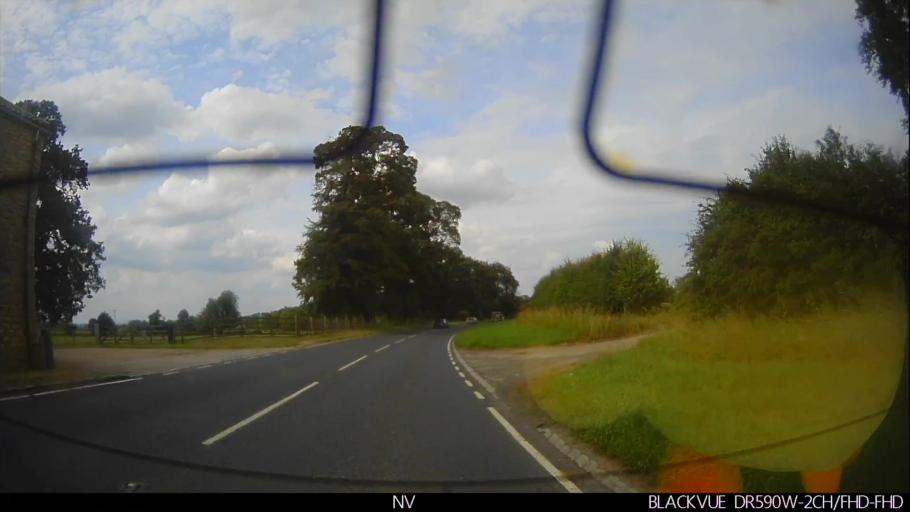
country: GB
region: England
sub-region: North Yorkshire
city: Marishes
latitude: 54.1683
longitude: -0.7659
